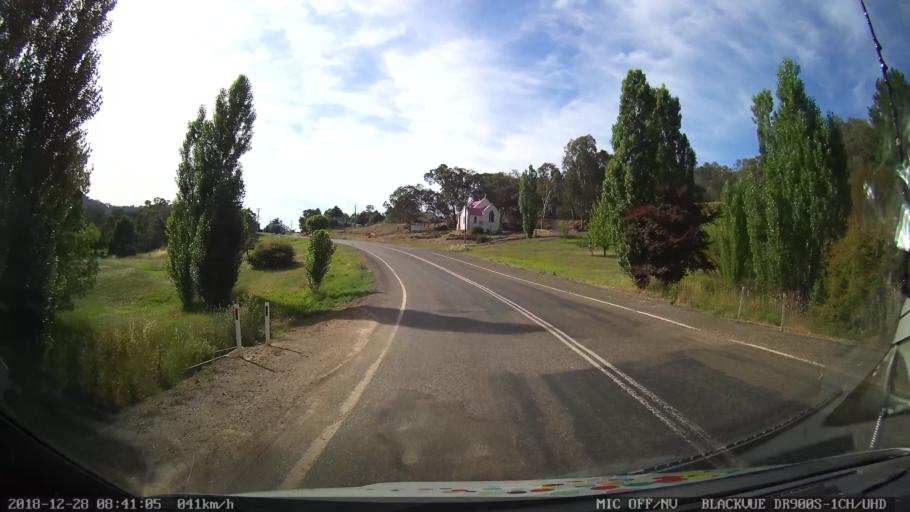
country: AU
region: New South Wales
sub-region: Upper Lachlan Shire
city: Crookwell
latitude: -34.0145
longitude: 149.3254
